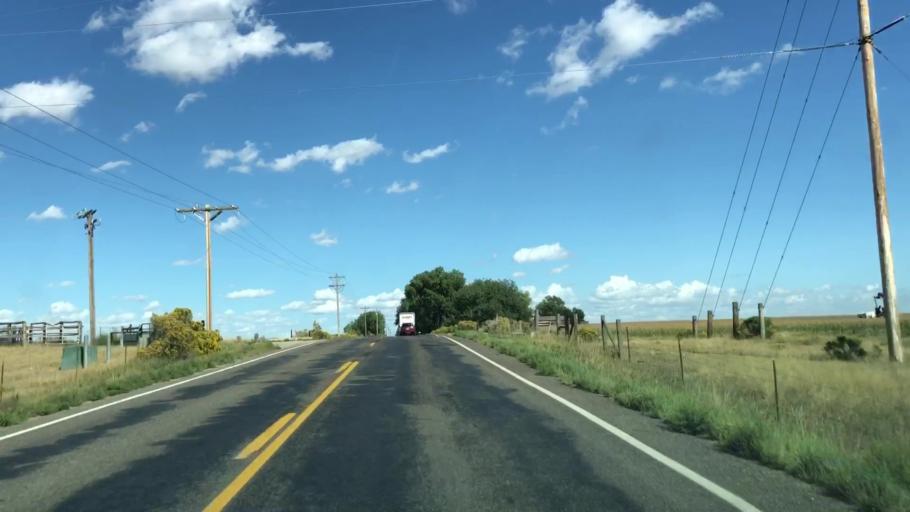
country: US
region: Colorado
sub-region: Larimer County
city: Wellington
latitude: 40.7547
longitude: -105.0485
